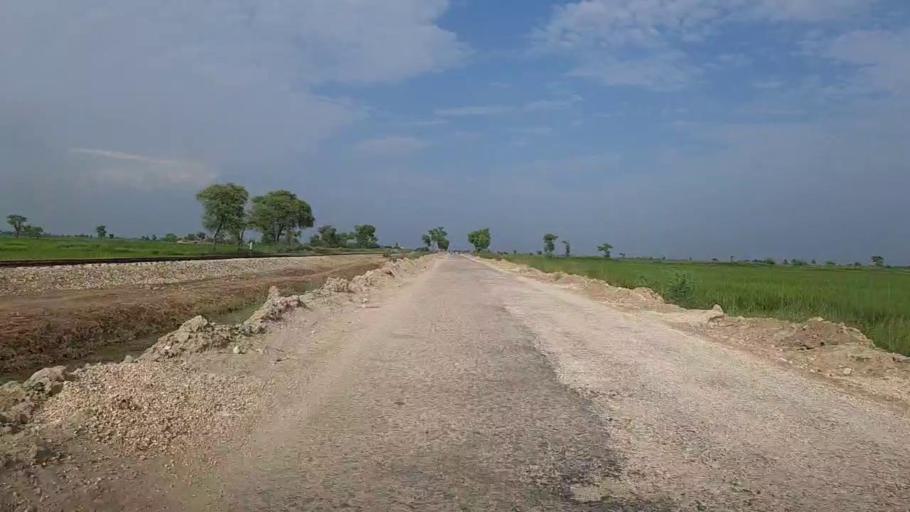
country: PK
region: Sindh
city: Thul
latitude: 28.2679
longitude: 68.8294
